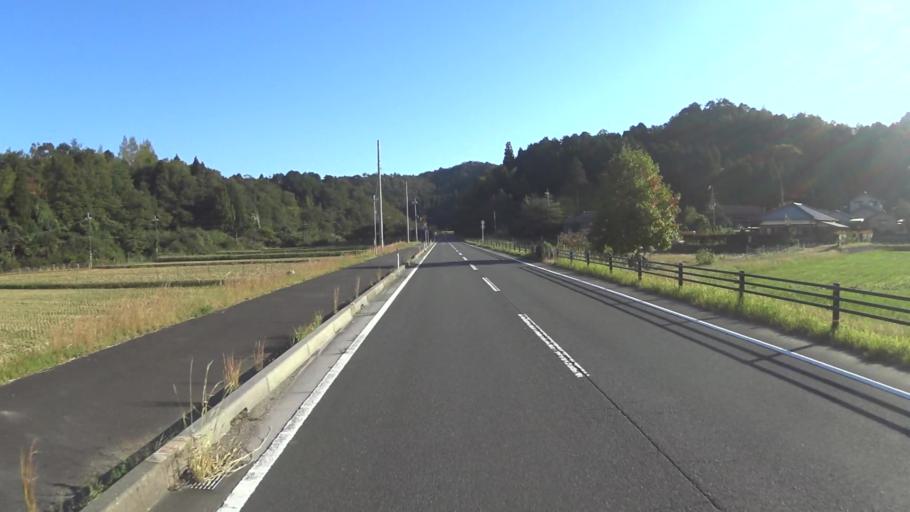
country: JP
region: Hyogo
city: Toyooka
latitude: 35.6272
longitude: 134.8877
